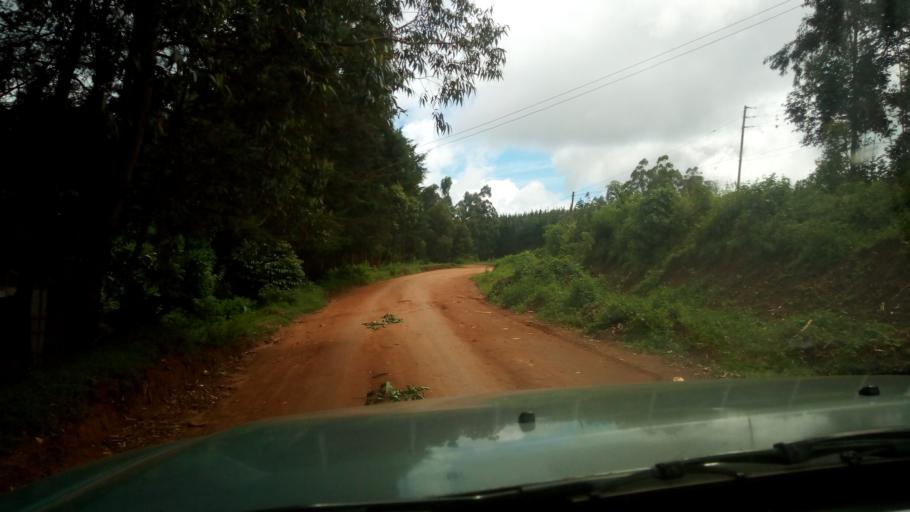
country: KE
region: Makueni
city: Wote
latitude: -1.6689
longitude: 37.4493
